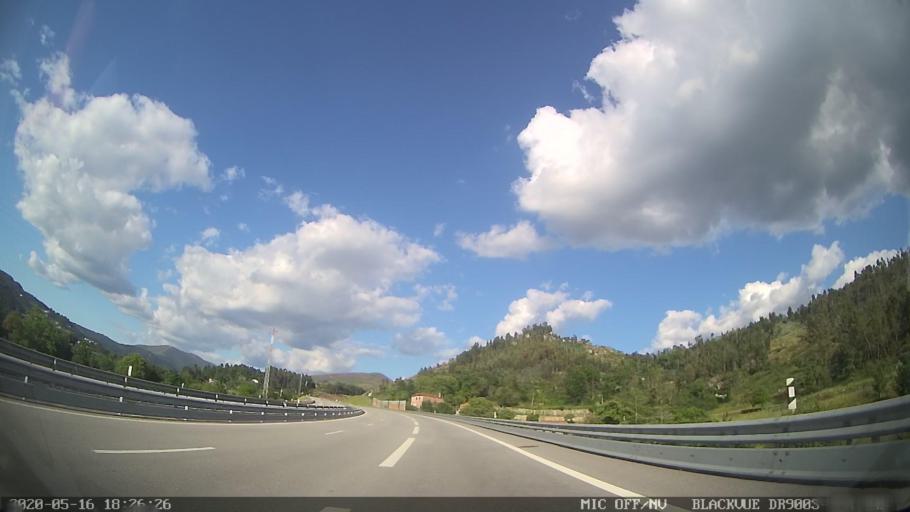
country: PT
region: Porto
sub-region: Amarante
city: Amarante
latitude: 41.2595
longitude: -8.0166
